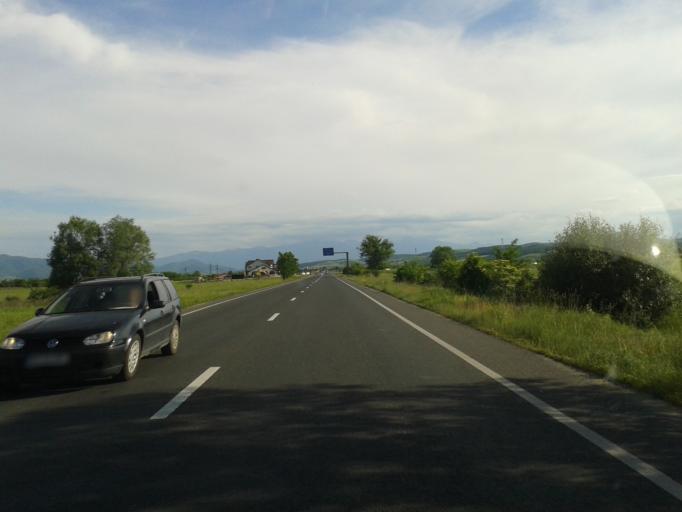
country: RO
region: Hunedoara
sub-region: Comuna Calan
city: Calan
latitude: 45.7291
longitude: 22.9961
